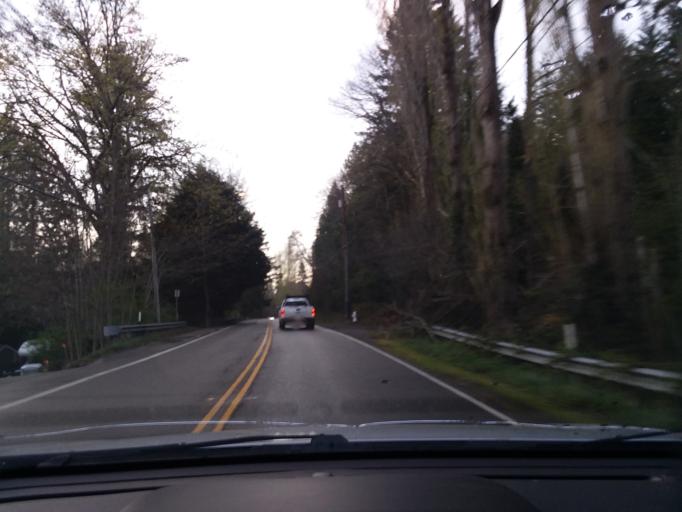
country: US
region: Washington
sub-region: King County
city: Kenmore
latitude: 47.7699
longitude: -122.2422
